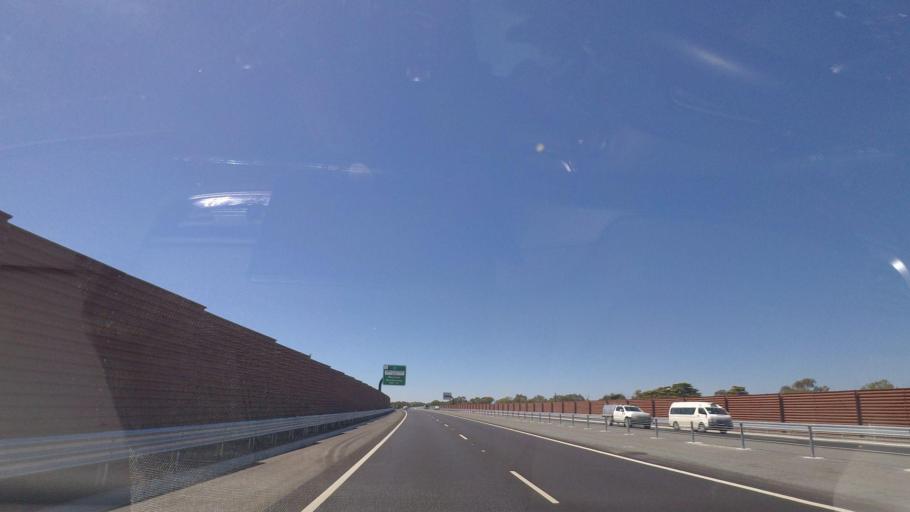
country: AU
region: Victoria
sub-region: Kingston
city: Waterways
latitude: -38.0020
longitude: 145.1231
